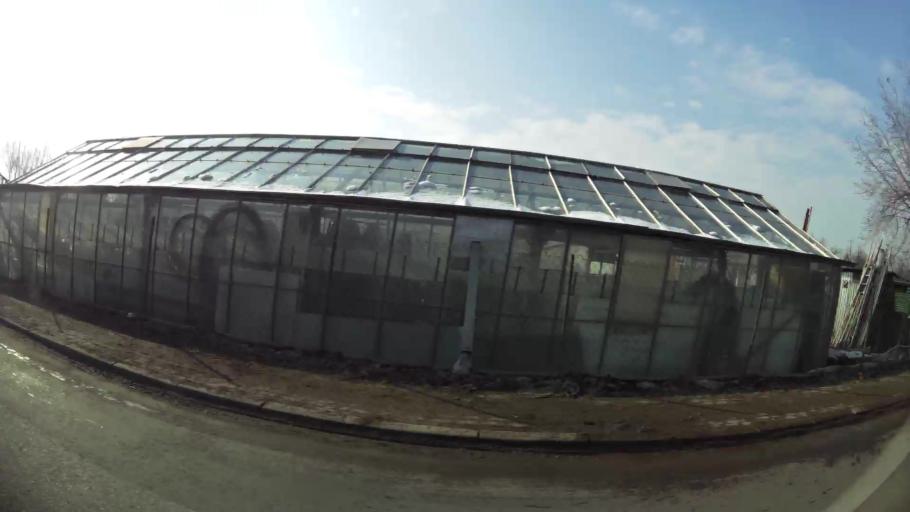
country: MK
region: Suto Orizari
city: Suto Orizare
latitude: 42.0234
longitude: 21.3854
